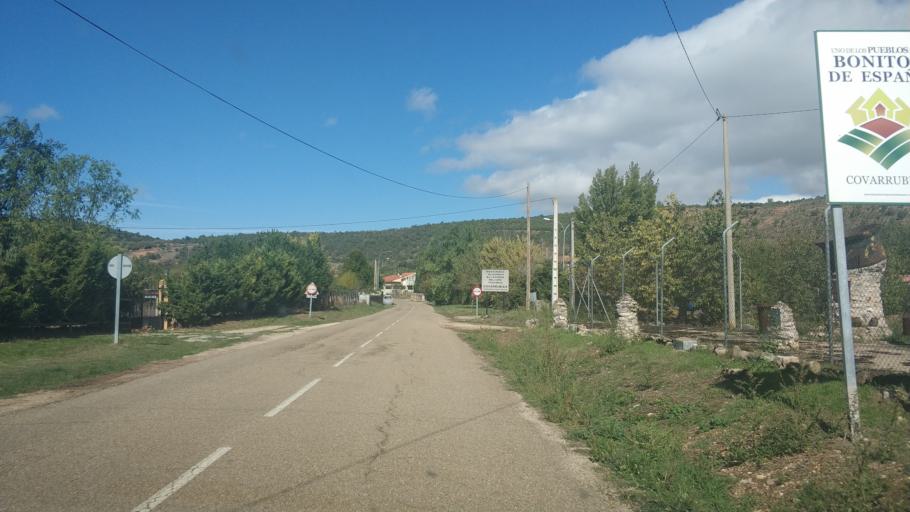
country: ES
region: Castille and Leon
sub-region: Provincia de Burgos
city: Covarrubias
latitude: 42.0578
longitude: -3.5130
